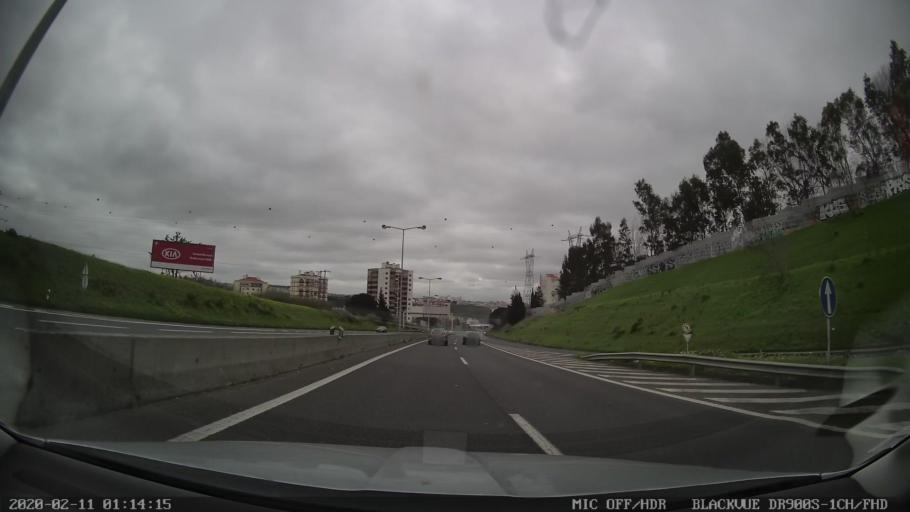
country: PT
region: Lisbon
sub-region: Odivelas
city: Povoa de Santo Adriao
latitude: 38.8007
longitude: -9.1766
